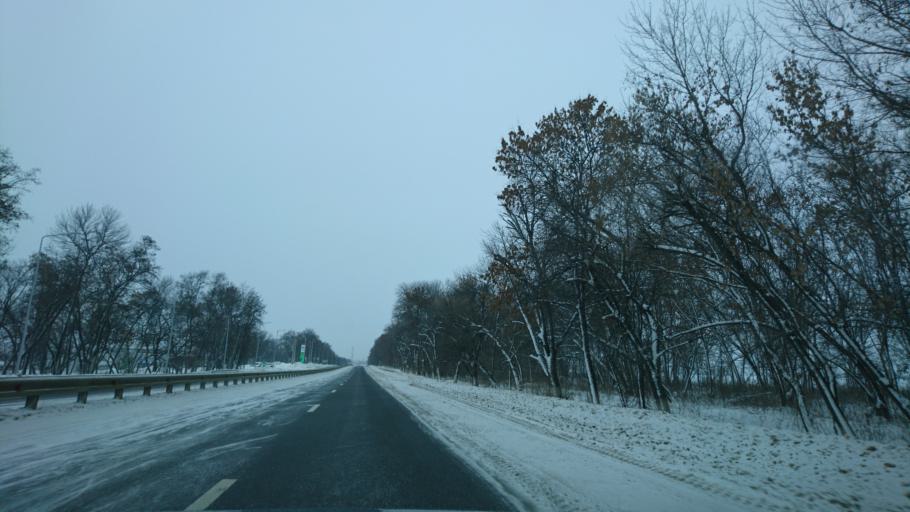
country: RU
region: Belgorod
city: Bessonovka
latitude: 50.3542
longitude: 36.3038
